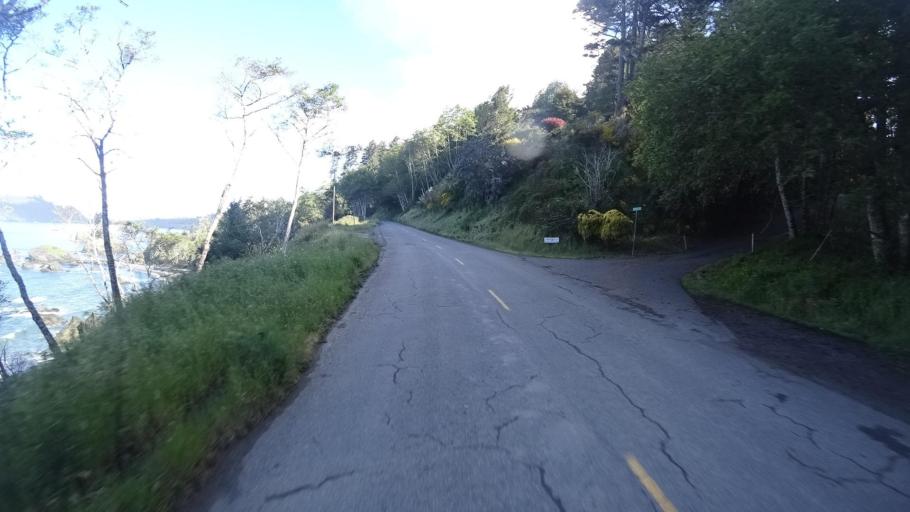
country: US
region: California
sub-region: Humboldt County
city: Westhaven-Moonstone
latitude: 41.0480
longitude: -124.1238
